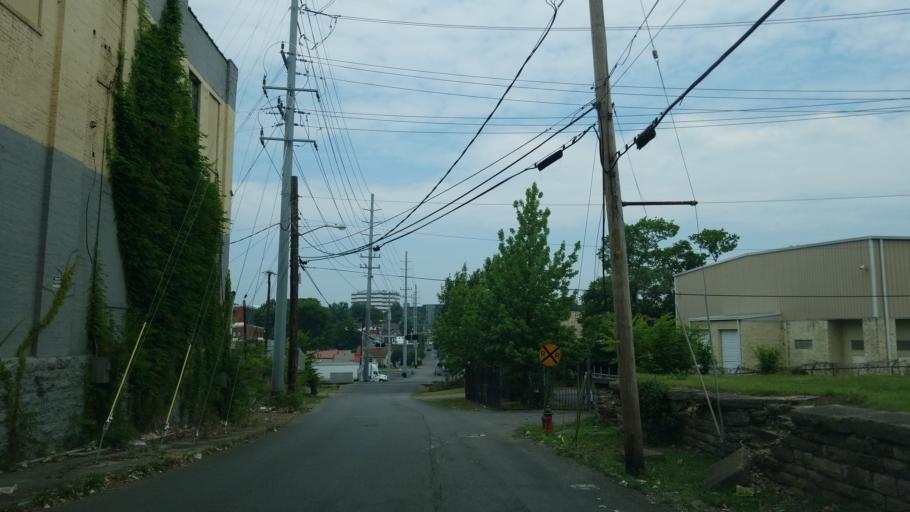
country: US
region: Tennessee
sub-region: Davidson County
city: Nashville
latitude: 36.1608
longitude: -86.8035
